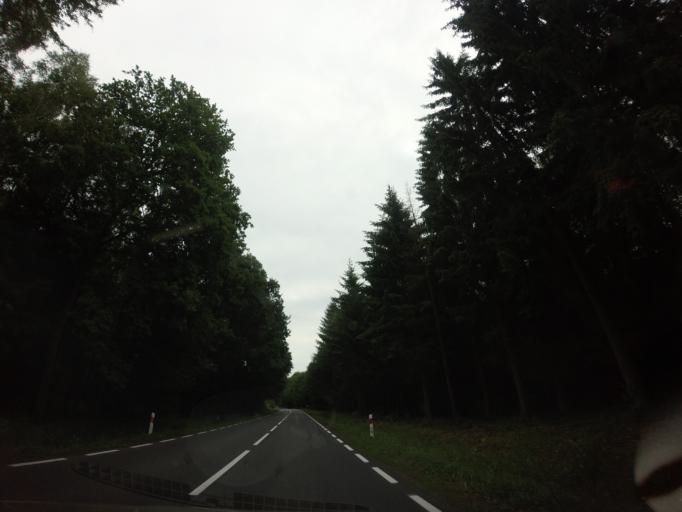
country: PL
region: West Pomeranian Voivodeship
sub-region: Powiat szczecinecki
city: Lubowo
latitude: 53.5901
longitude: 16.3284
